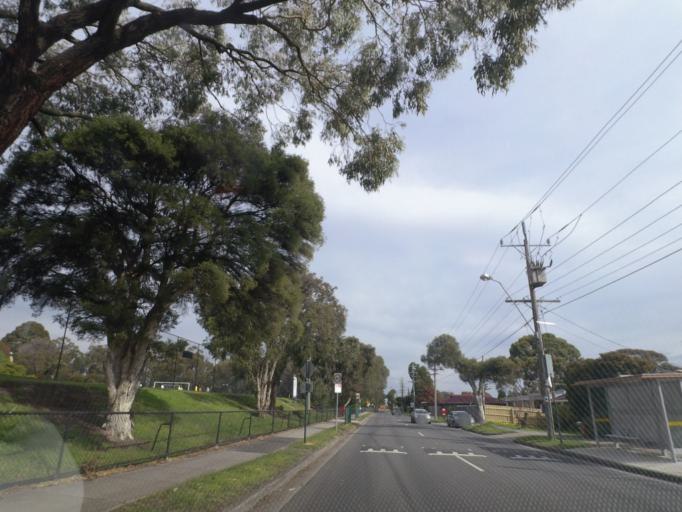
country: AU
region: Victoria
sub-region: Whitehorse
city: Vermont
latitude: -37.8431
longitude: 145.1997
